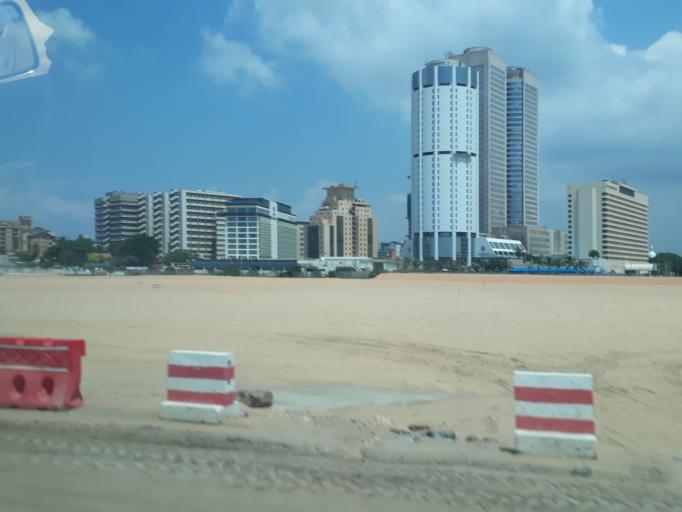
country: LK
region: Western
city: Colombo
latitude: 6.9305
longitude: 79.8394
